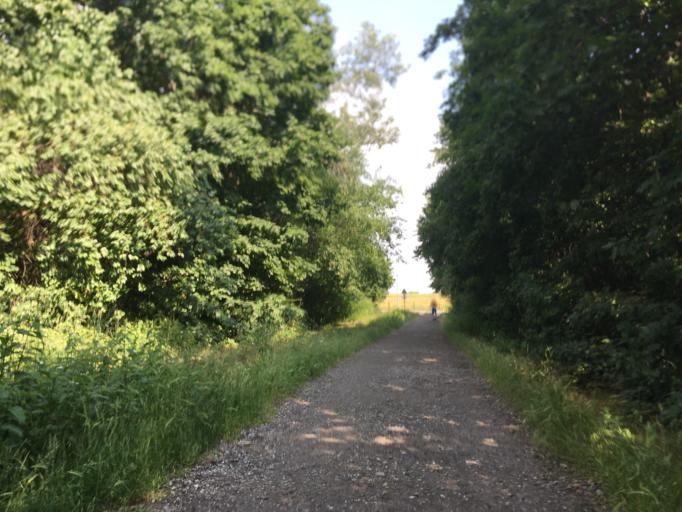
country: DE
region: Berlin
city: Lubars
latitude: 52.6129
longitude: 13.3652
